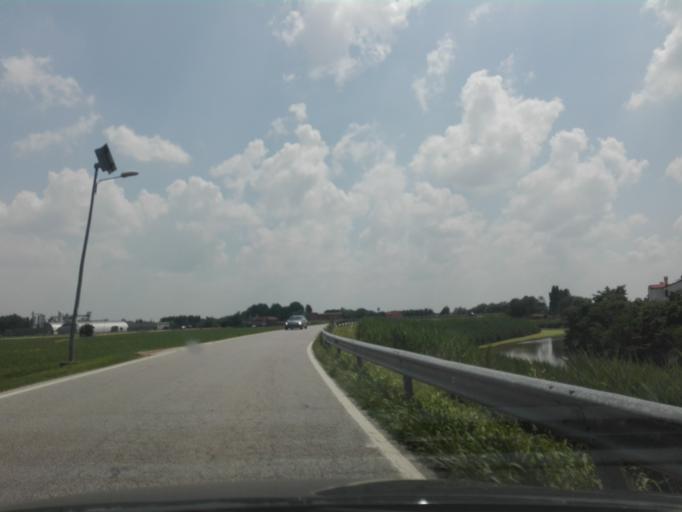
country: IT
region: Veneto
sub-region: Provincia di Rovigo
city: Adria
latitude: 45.0559
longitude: 12.0204
